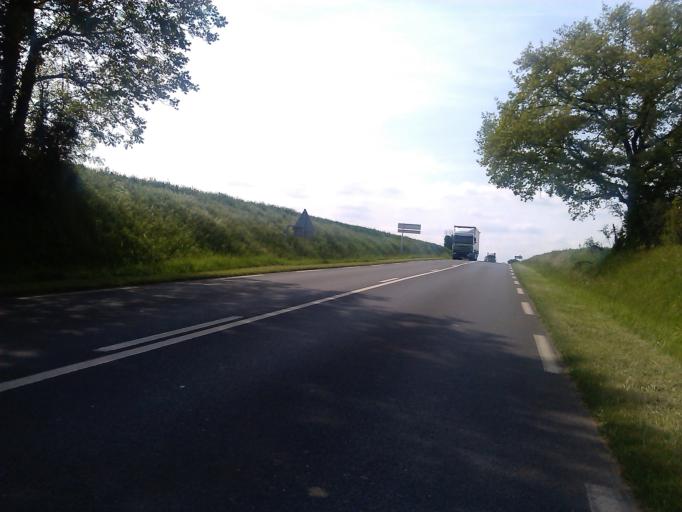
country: FR
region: Centre
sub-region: Departement de l'Indre
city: La Chatre
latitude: 46.5632
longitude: 2.0458
